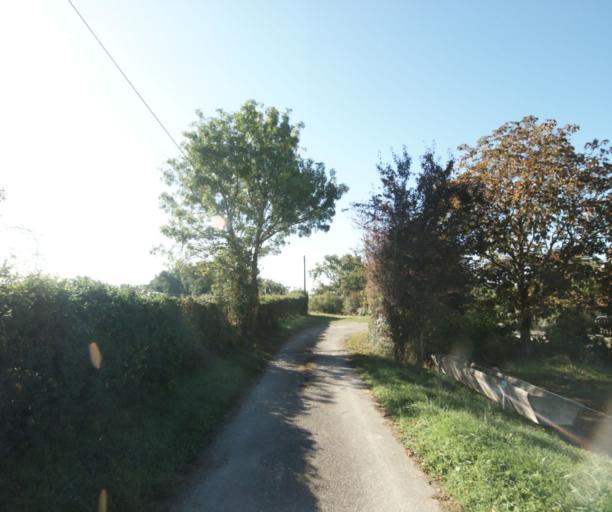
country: FR
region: Midi-Pyrenees
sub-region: Departement du Gers
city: Gondrin
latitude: 43.8208
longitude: 0.2569
